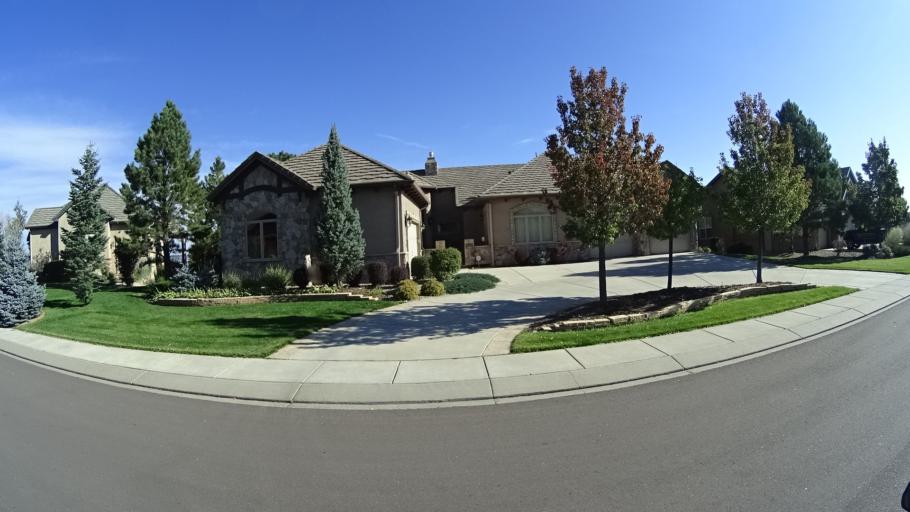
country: US
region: Colorado
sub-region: El Paso County
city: Colorado Springs
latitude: 38.8989
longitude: -104.7984
